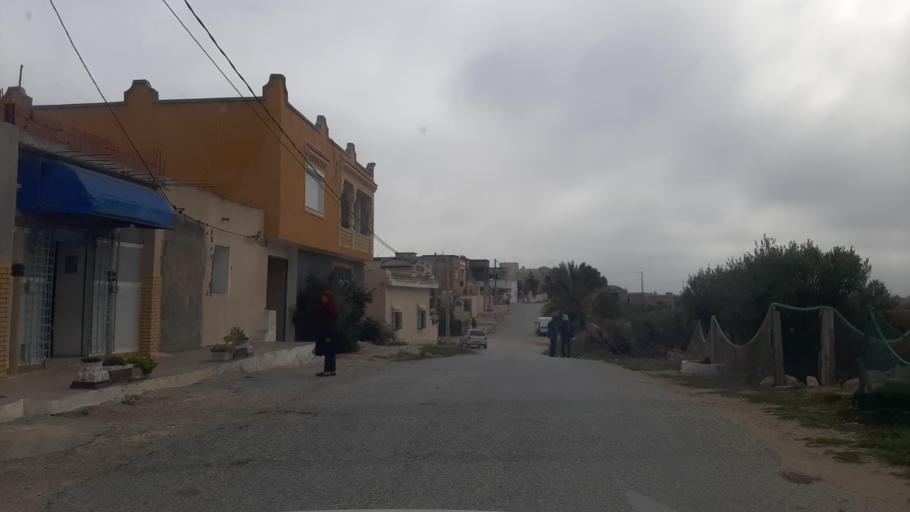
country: TN
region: Nabul
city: Menzel Heurr
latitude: 36.6767
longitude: 10.9227
